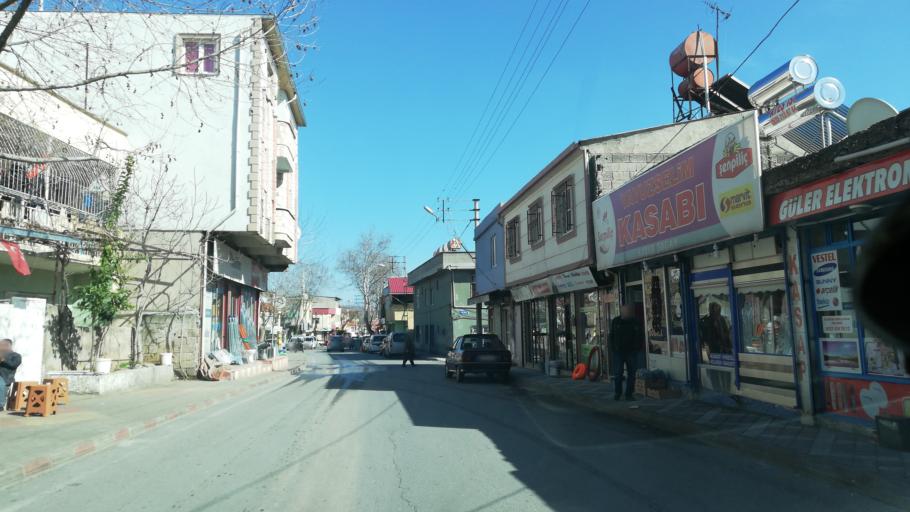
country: TR
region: Kahramanmaras
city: Kahramanmaras
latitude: 37.5747
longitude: 36.9481
